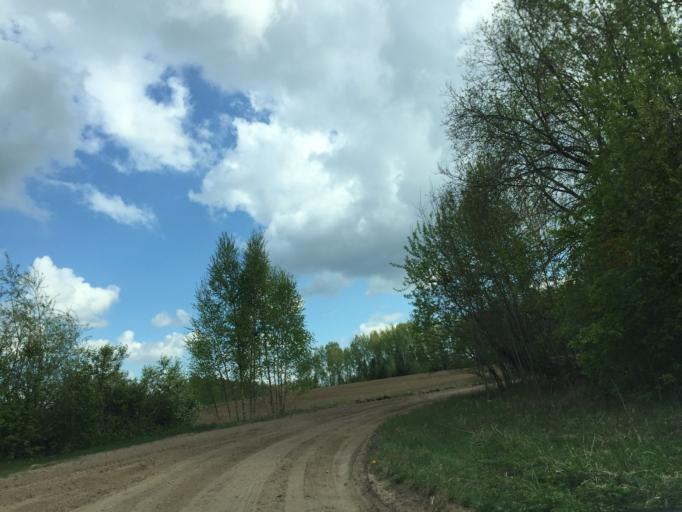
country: LV
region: Pargaujas
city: Stalbe
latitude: 57.3198
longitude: 24.8769
